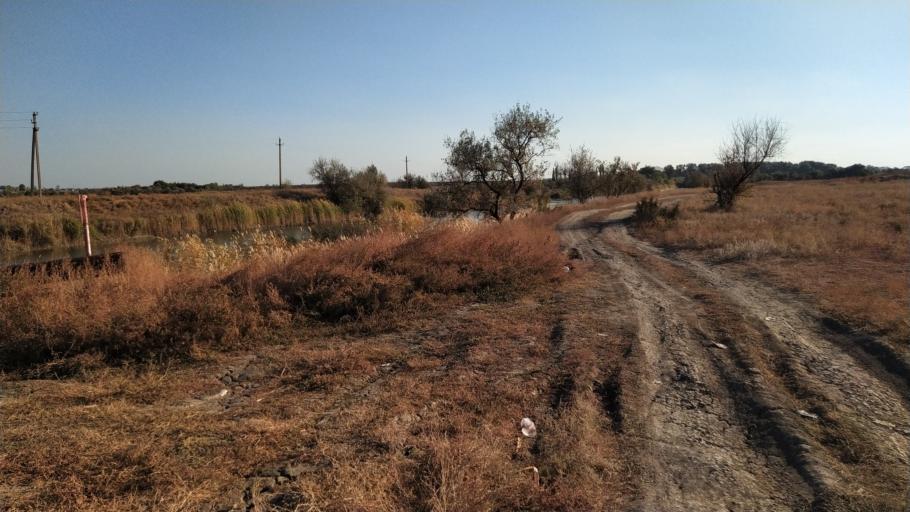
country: RU
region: Rostov
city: Kuleshovka
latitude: 47.1163
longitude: 39.6199
